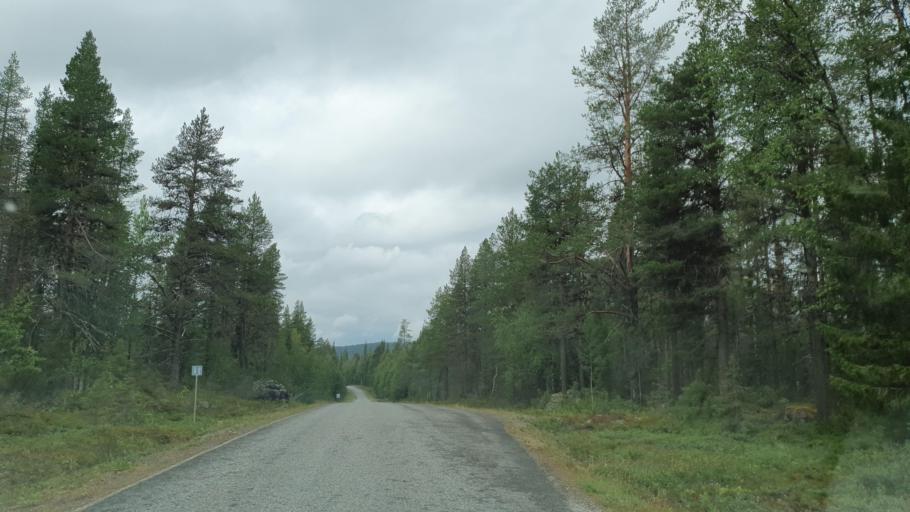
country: FI
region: Lapland
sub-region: Tunturi-Lappi
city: Kittilae
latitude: 67.7395
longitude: 24.3122
